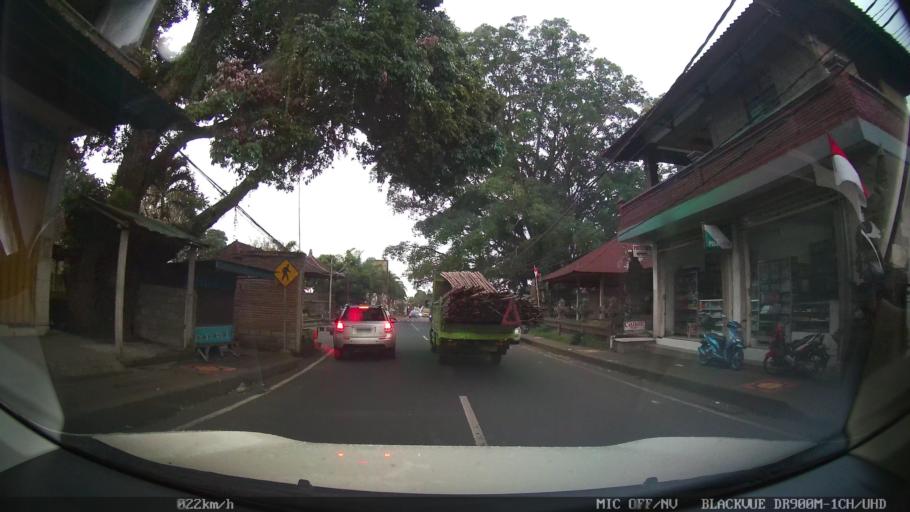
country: ID
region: Bali
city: Badung
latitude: -8.4321
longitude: 115.2454
